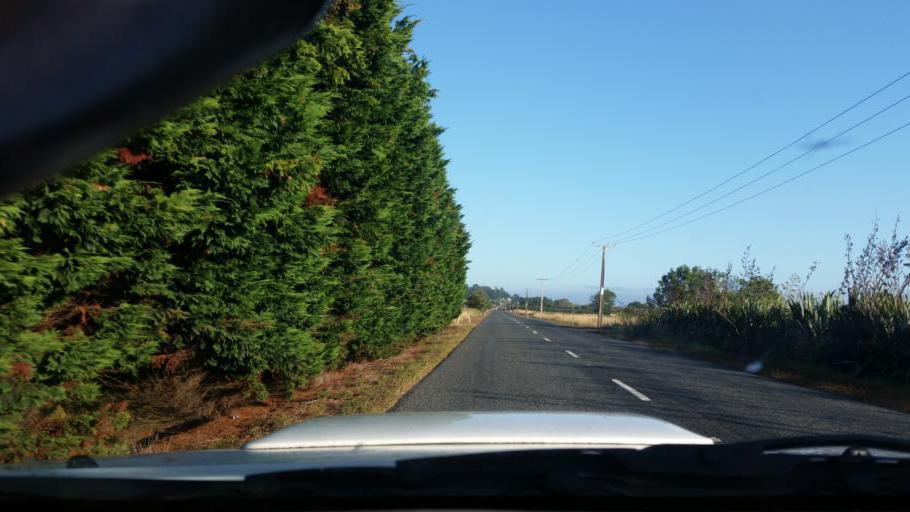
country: NZ
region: Northland
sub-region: Kaipara District
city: Dargaville
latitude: -35.9837
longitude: 173.8805
